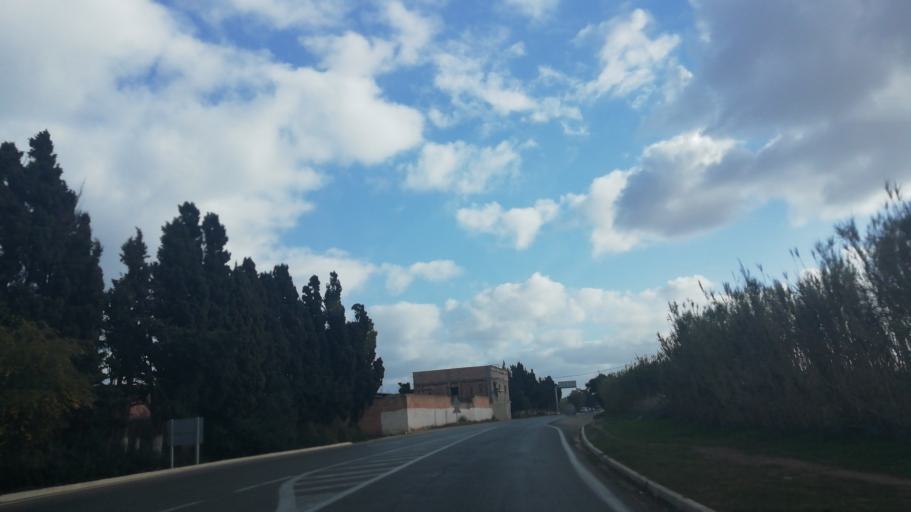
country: DZ
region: Relizane
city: Mazouna
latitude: 36.2456
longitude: 0.5378
